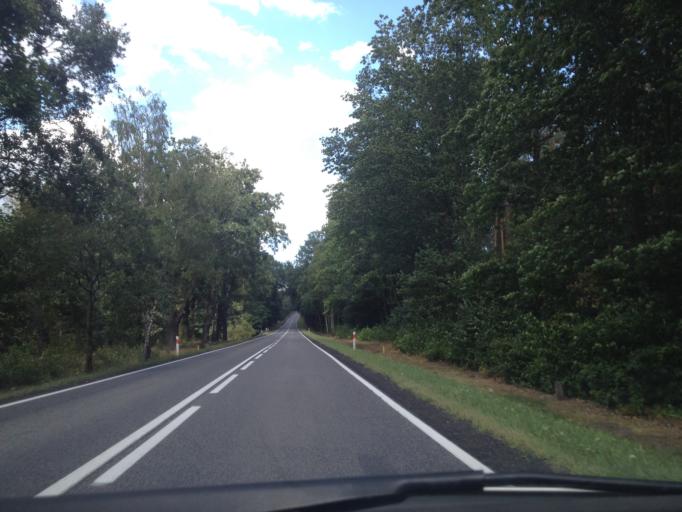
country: PL
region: Lubusz
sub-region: Powiat zarski
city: Sieniawa Zarska
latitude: 51.5788
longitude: 15.0652
